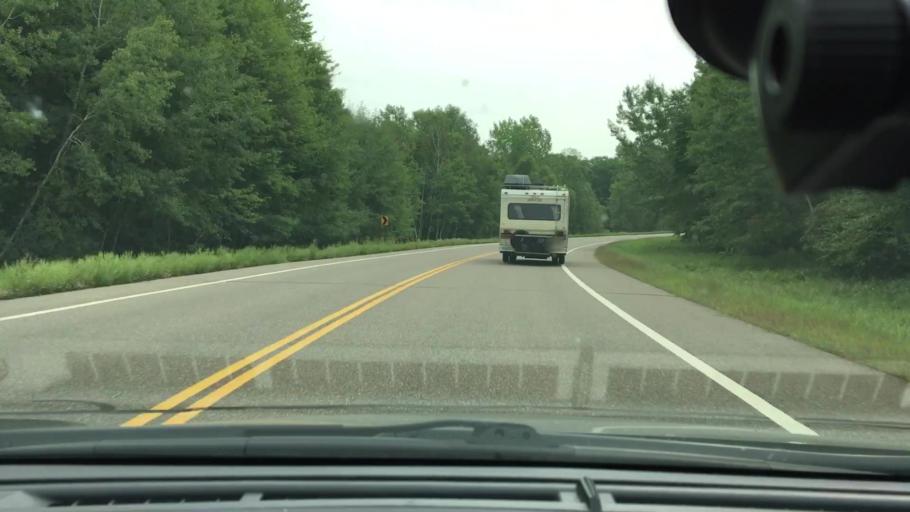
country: US
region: Minnesota
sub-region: Crow Wing County
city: Crosby
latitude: 46.4116
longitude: -93.8268
